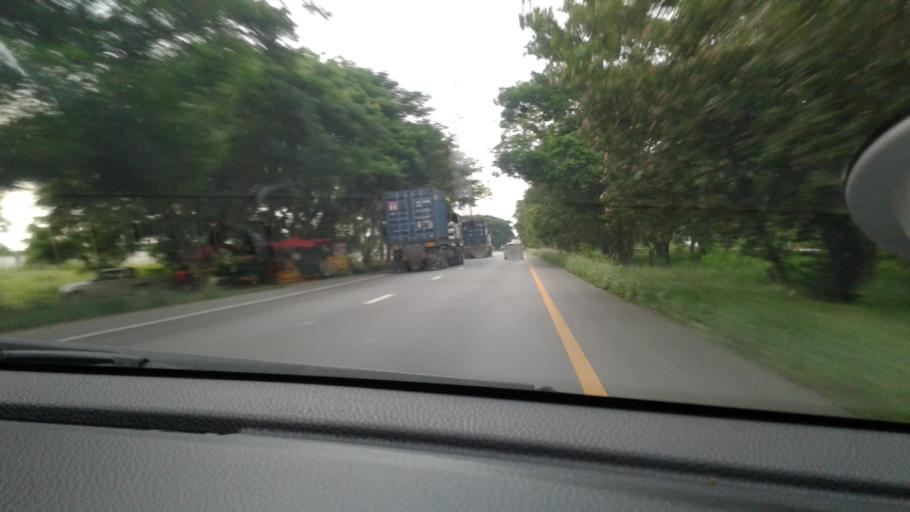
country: TH
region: Prachuap Khiri Khan
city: Hua Hin
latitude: 12.5234
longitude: 99.8806
